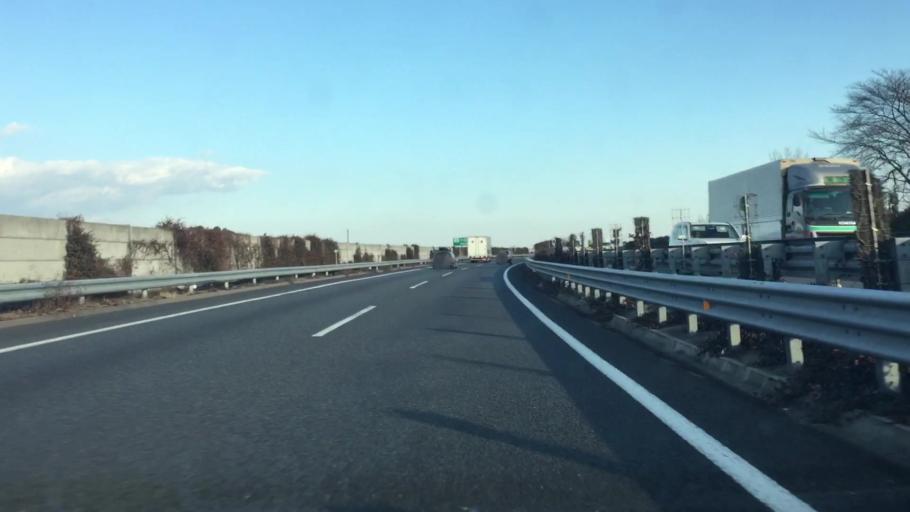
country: JP
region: Gunma
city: Ota
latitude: 36.3366
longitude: 139.3646
